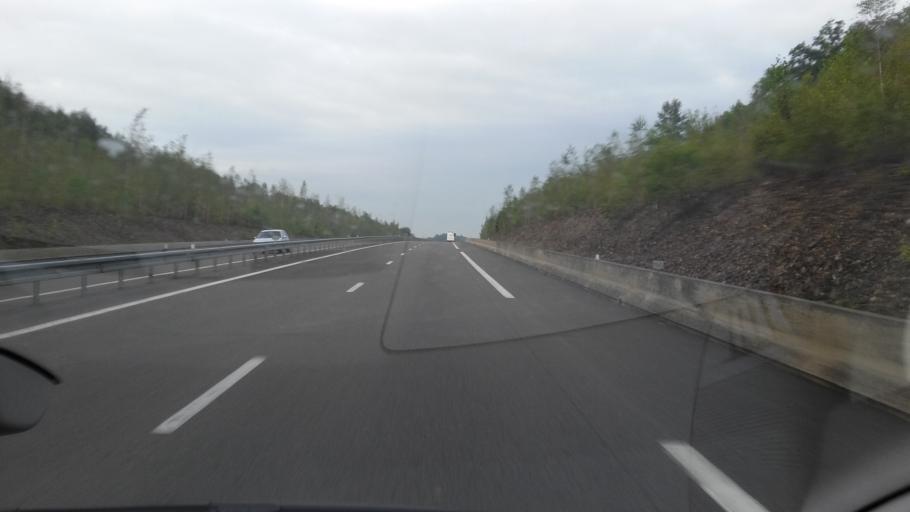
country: FR
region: Champagne-Ardenne
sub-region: Departement des Ardennes
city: Attigny
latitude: 49.6119
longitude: 4.5368
